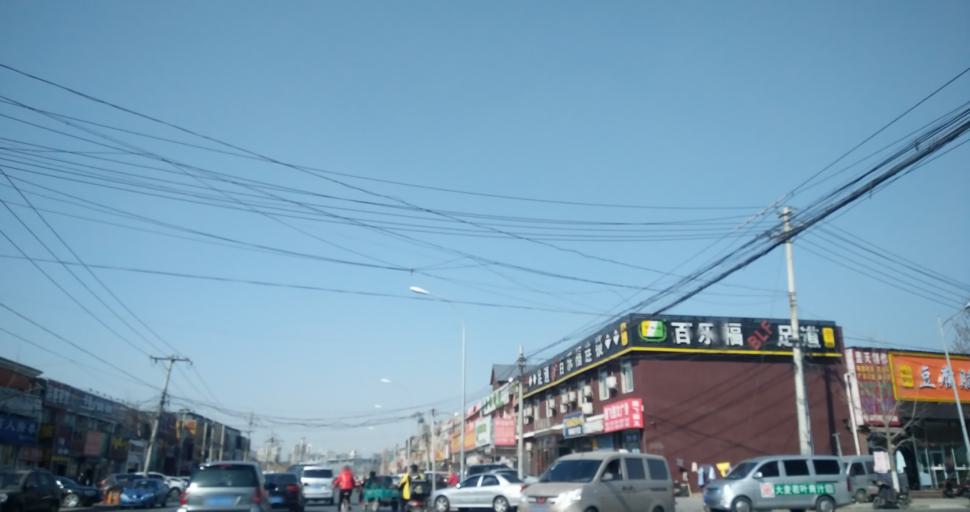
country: CN
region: Beijing
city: Jiugong
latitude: 39.8066
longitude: 116.4376
